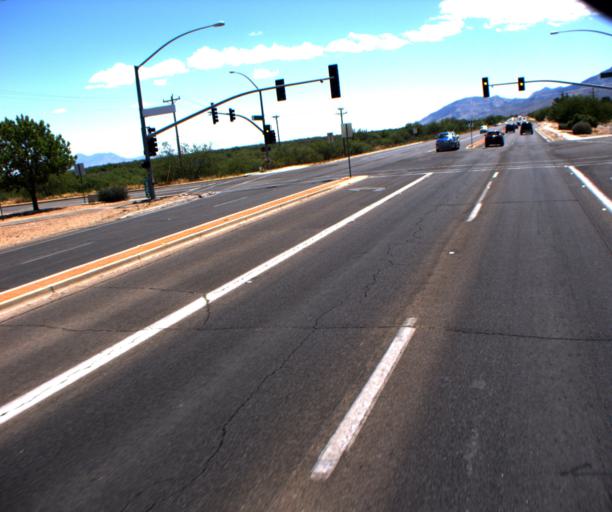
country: US
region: Arizona
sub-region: Cochise County
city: Sierra Vista
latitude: 31.5290
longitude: -110.2574
